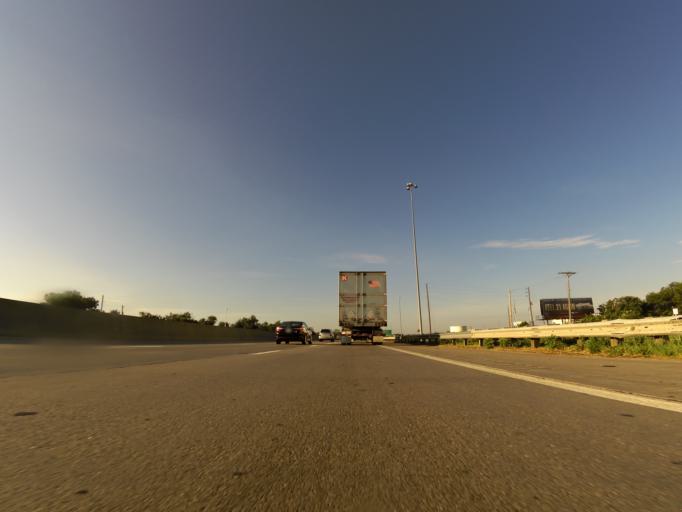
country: US
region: Kansas
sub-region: Sedgwick County
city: Wichita
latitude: 37.7307
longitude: -97.3170
